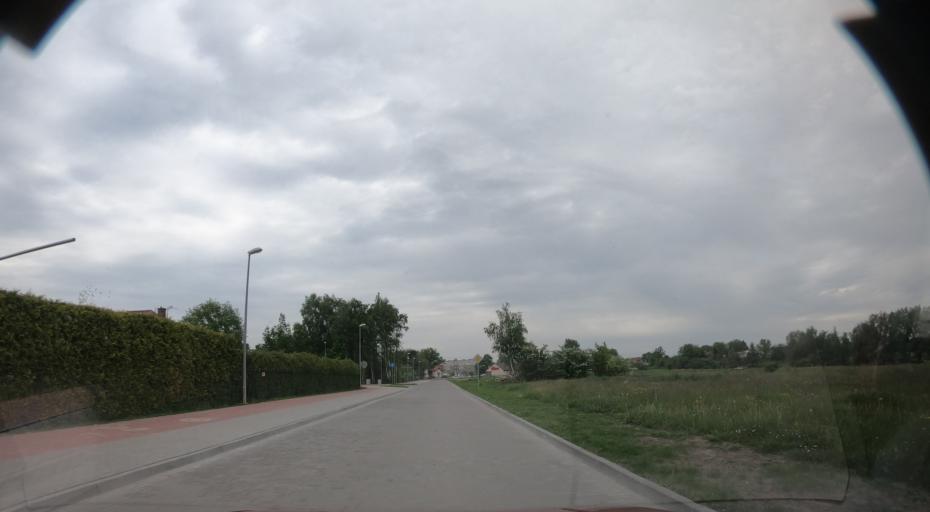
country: PL
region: West Pomeranian Voivodeship
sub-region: Powiat kolobrzeski
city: Kolobrzeg
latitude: 54.1491
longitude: 15.5574
